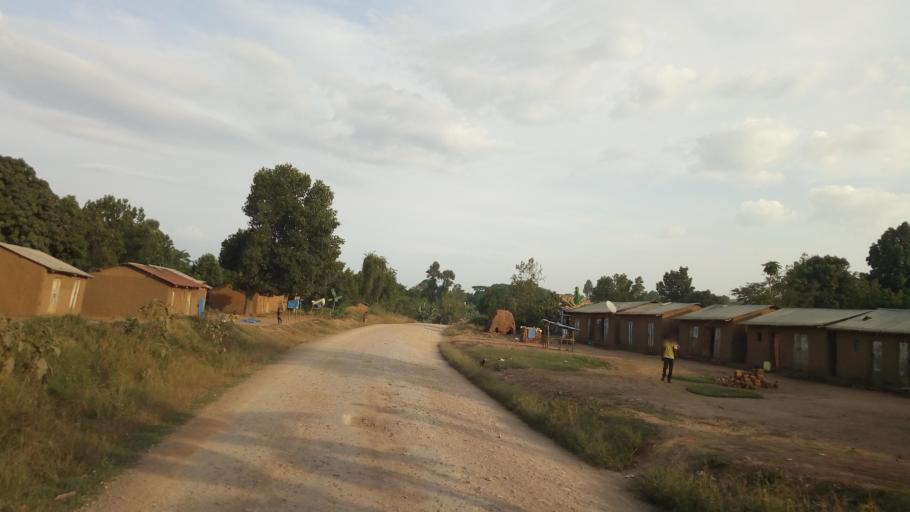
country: UG
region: Central Region
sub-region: Kiboga District
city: Kiboga
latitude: 0.7061
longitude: 31.7762
